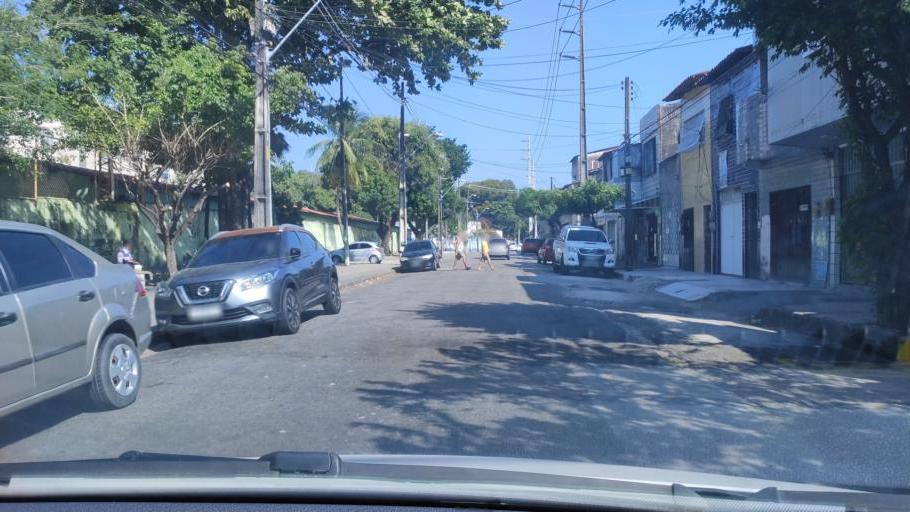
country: BR
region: Ceara
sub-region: Fortaleza
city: Fortaleza
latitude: -3.7422
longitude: -38.5350
